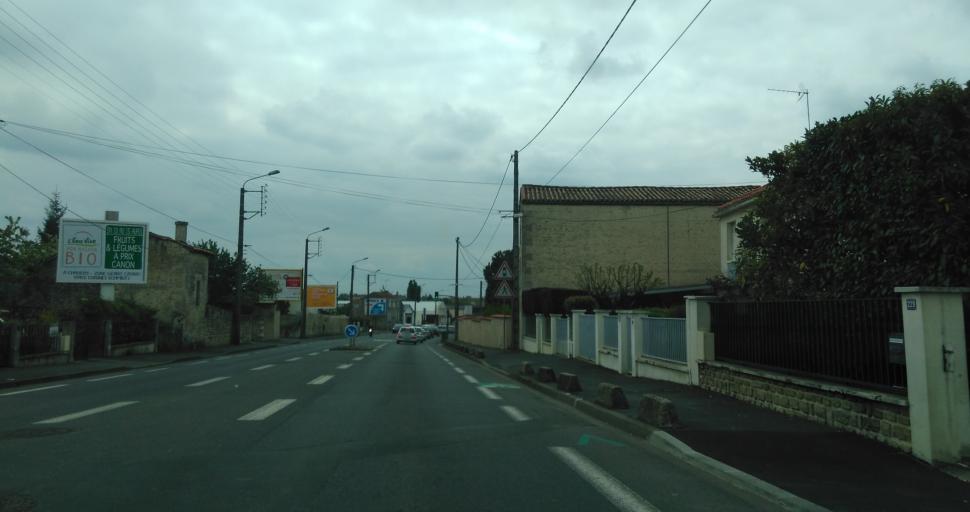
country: FR
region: Poitou-Charentes
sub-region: Departement des Deux-Sevres
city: Niort
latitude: 46.3402
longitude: -0.4458
